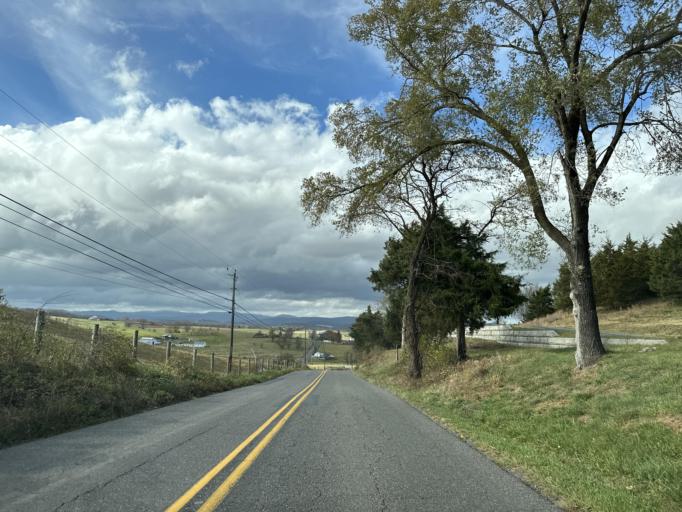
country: US
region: Virginia
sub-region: City of Harrisonburg
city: Harrisonburg
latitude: 38.4719
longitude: -78.8871
